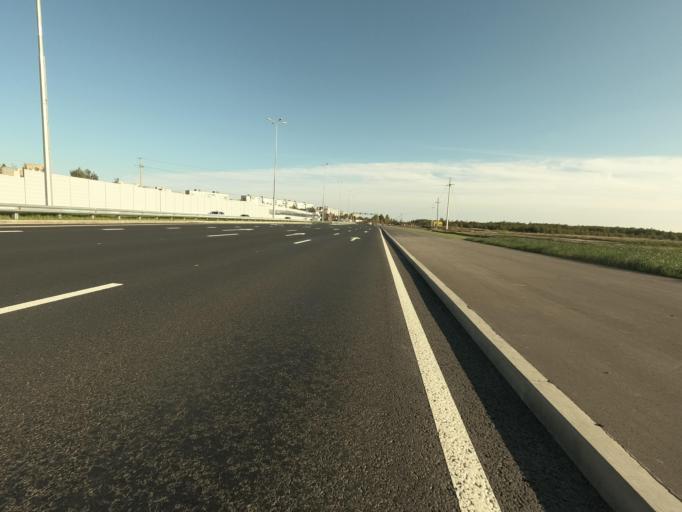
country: RU
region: St.-Petersburg
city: Kolpino
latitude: 59.7379
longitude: 30.5536
